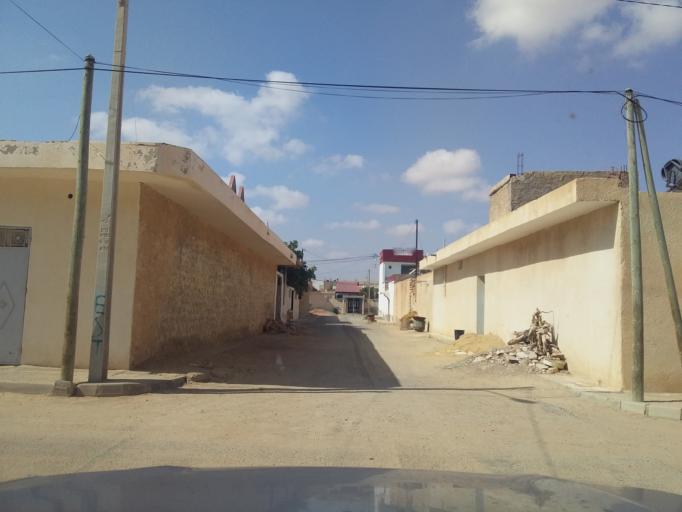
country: TN
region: Madanin
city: Medenine
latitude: 33.5828
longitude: 10.3243
